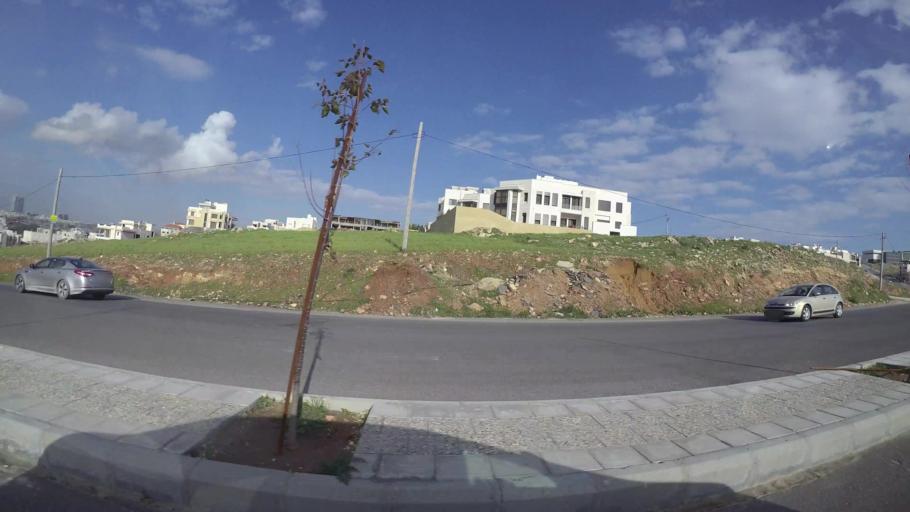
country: JO
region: Amman
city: Wadi as Sir
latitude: 31.9241
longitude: 35.8476
